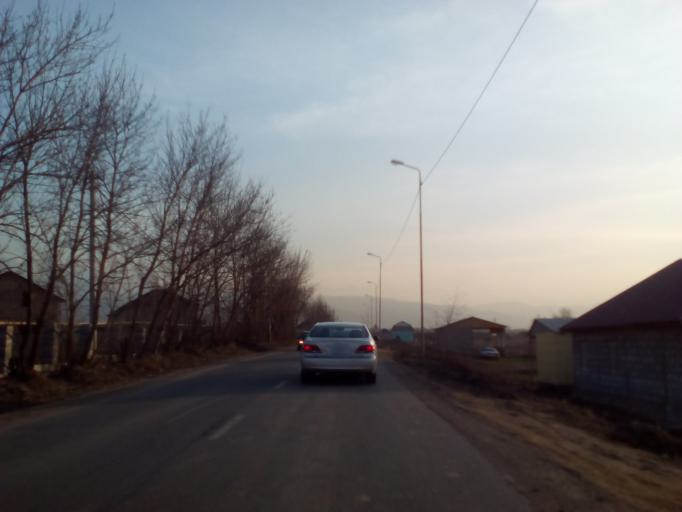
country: KZ
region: Almaty Oblysy
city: Burunday
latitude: 43.2377
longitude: 76.7434
